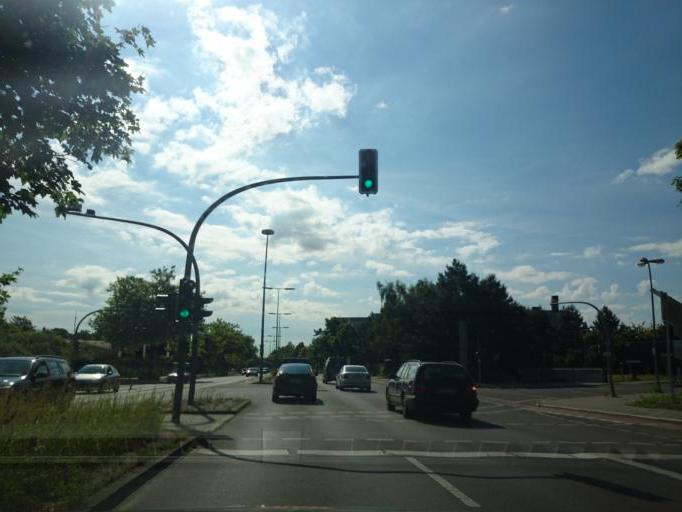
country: DE
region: Berlin
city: Marienfelde
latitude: 52.4108
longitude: 13.3660
